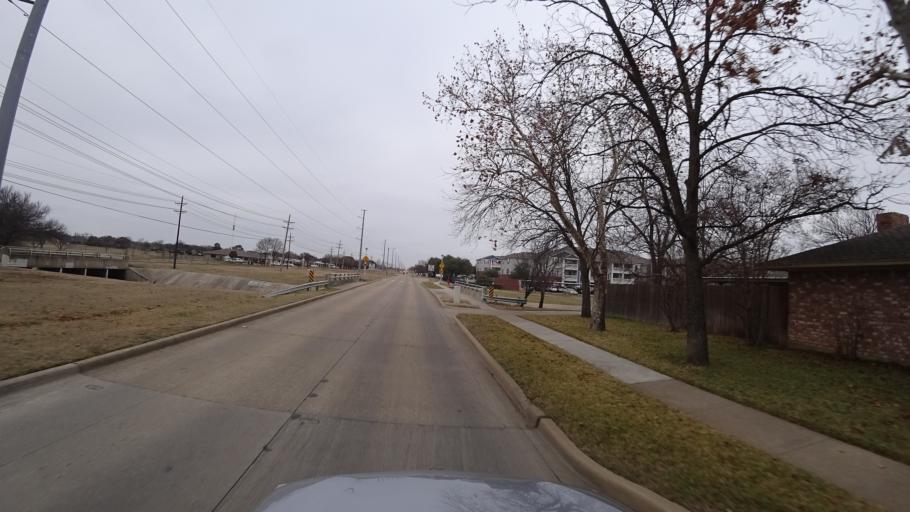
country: US
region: Texas
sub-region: Denton County
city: Highland Village
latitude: 33.0528
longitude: -97.0354
